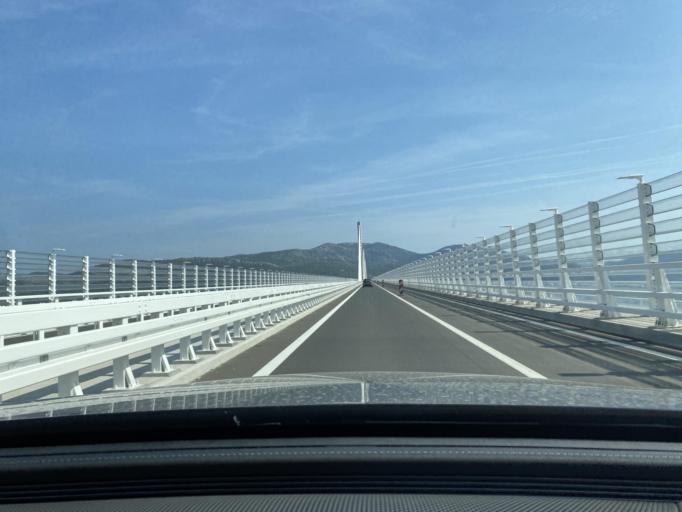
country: BA
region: Federation of Bosnia and Herzegovina
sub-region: Hercegovacko-Bosanski Kanton
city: Neum
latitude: 42.9239
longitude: 17.5285
